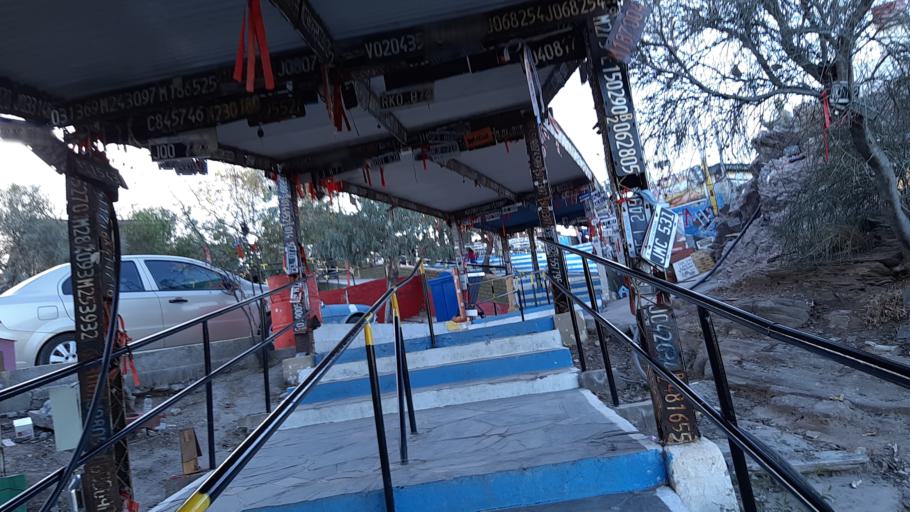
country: AR
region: San Juan
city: Caucete
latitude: -31.7349
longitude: -67.9825
